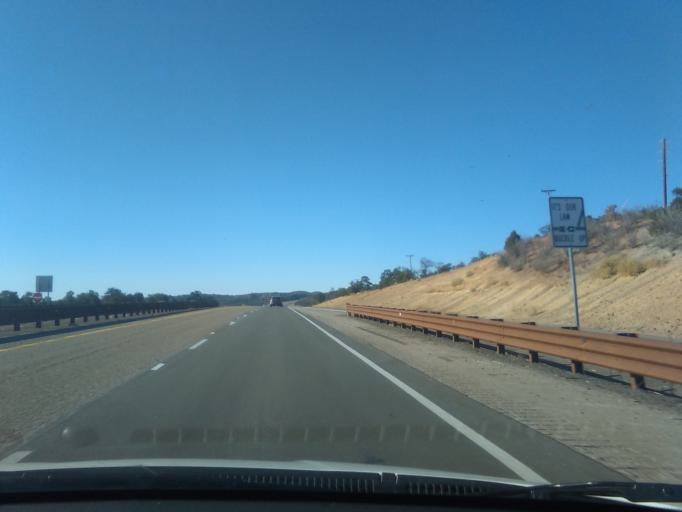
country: US
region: New Mexico
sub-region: Santa Fe County
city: Eldorado at Santa Fe
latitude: 35.5472
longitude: -105.8294
